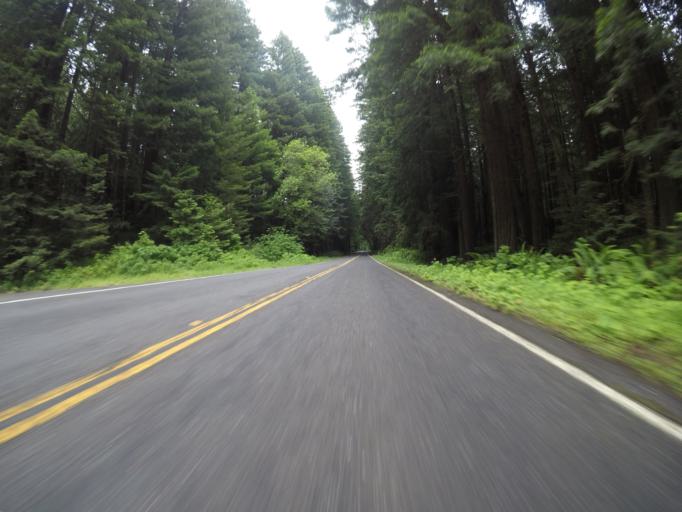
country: US
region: California
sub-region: Humboldt County
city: Rio Dell
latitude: 40.4461
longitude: -124.0149
